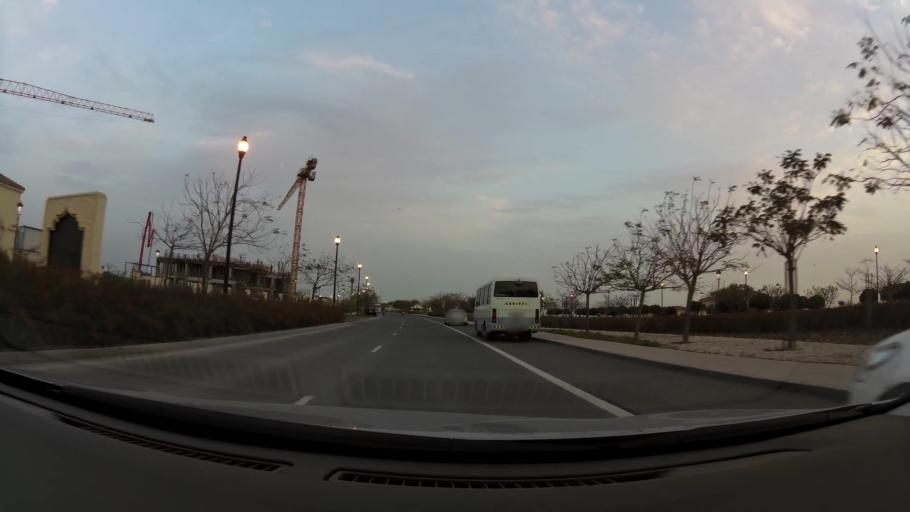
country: QA
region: Baladiyat ad Dawhah
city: Doha
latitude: 25.3612
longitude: 51.5661
